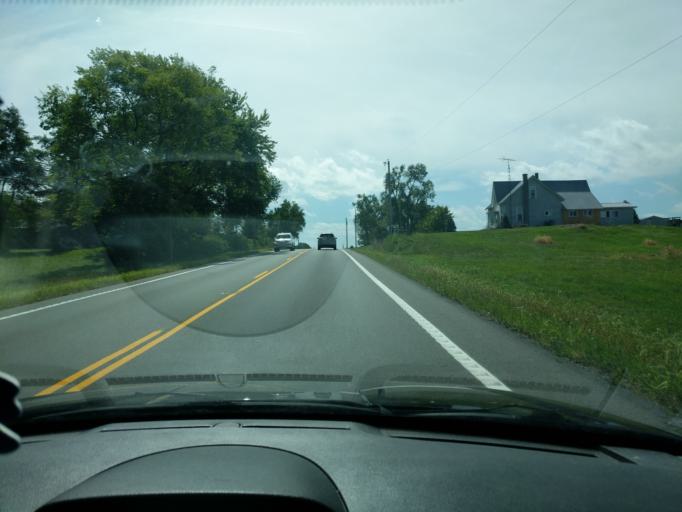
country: US
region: Ohio
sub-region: Logan County
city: Bellefontaine
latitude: 40.3113
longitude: -83.7600
